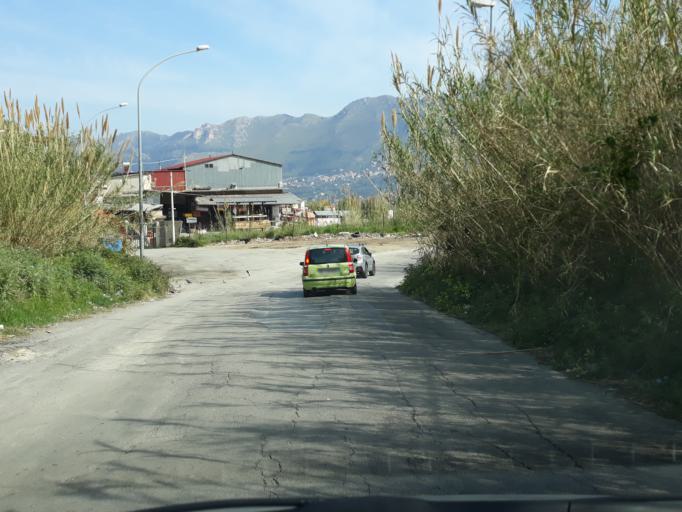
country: IT
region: Sicily
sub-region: Palermo
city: Monreale
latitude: 38.0743
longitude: 13.2823
